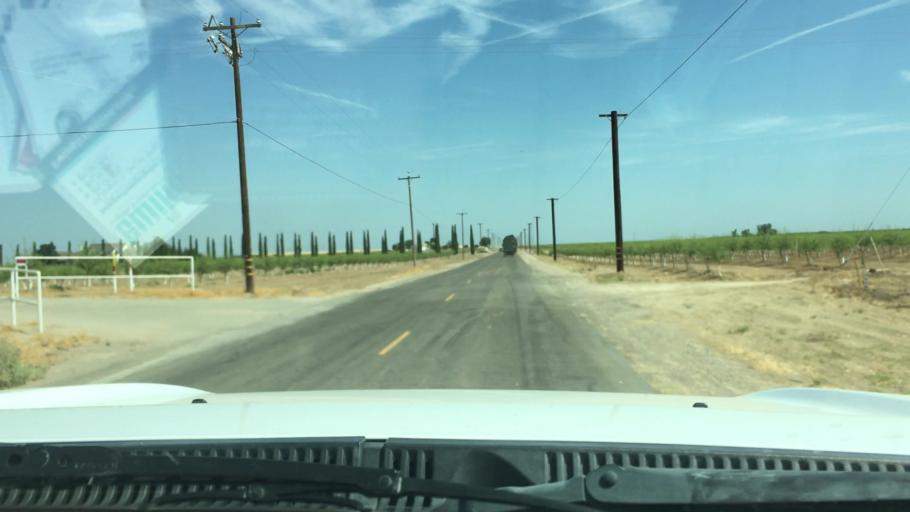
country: US
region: California
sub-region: Kern County
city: Shafter
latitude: 35.4562
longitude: -119.3681
